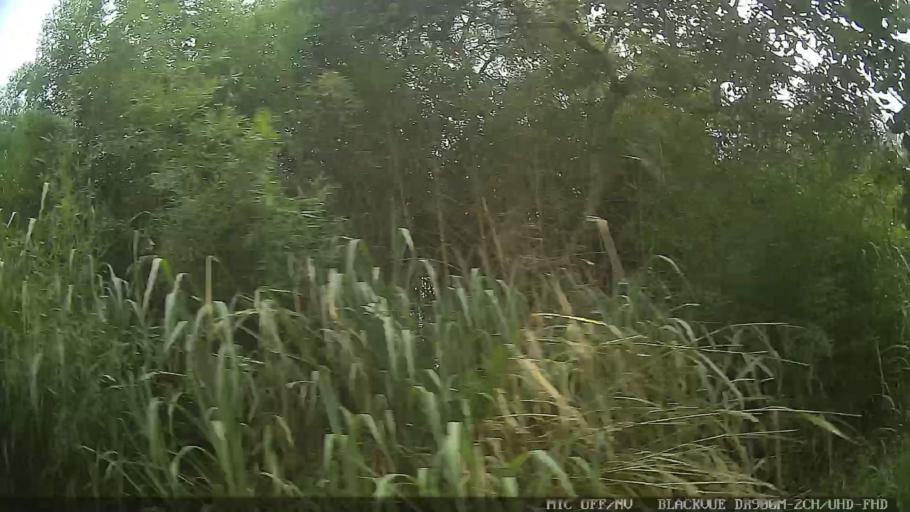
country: BR
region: Sao Paulo
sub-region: Mogi das Cruzes
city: Mogi das Cruzes
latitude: -23.4352
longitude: -46.2284
